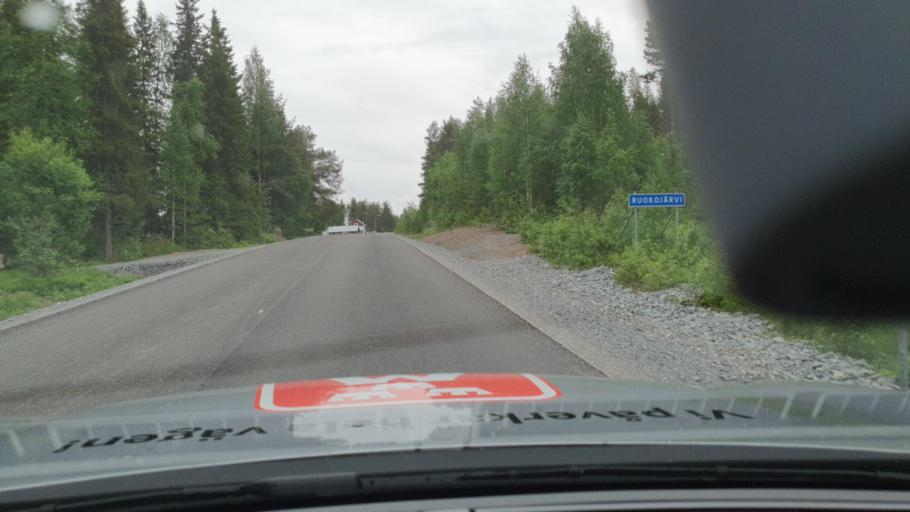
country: SE
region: Norrbotten
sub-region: Overtornea Kommun
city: OEvertornea
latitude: 66.6200
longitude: 23.2875
